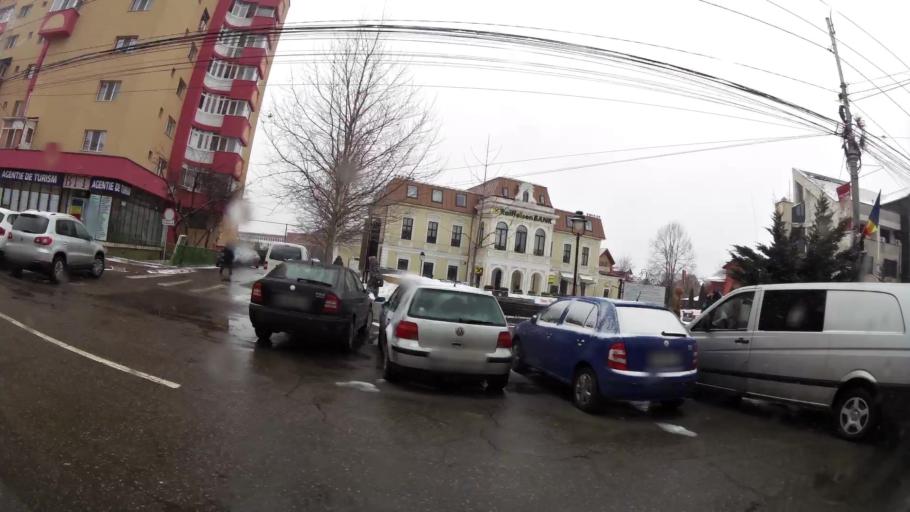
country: RO
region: Dambovita
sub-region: Municipiul Targoviste
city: Targoviste
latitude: 44.9251
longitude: 25.4599
